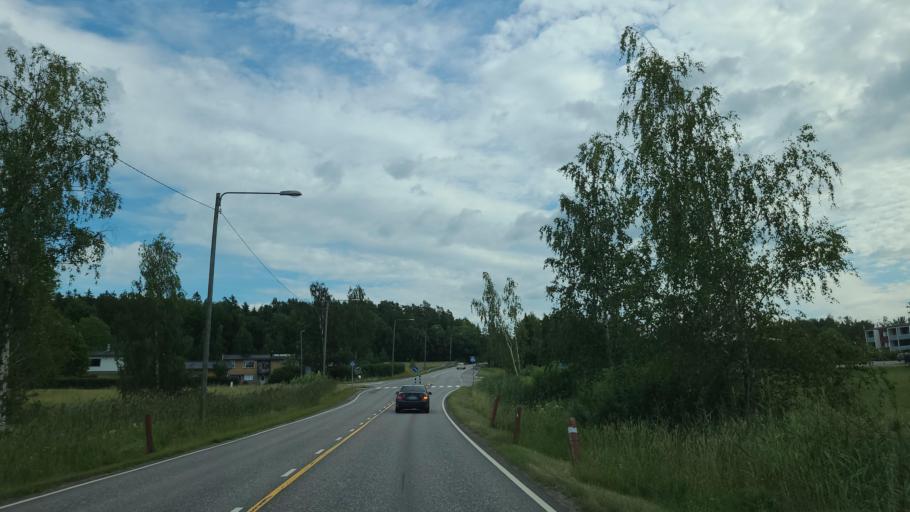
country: FI
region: Varsinais-Suomi
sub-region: Turku
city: Rymaettylae
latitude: 60.3777
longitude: 21.9454
